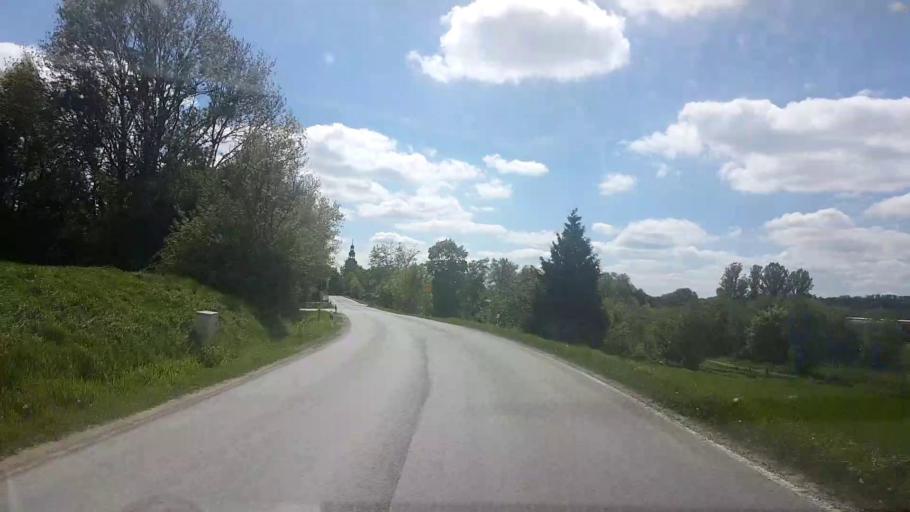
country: DE
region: Bavaria
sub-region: Upper Franconia
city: Grossheirath
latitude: 50.1815
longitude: 10.9523
